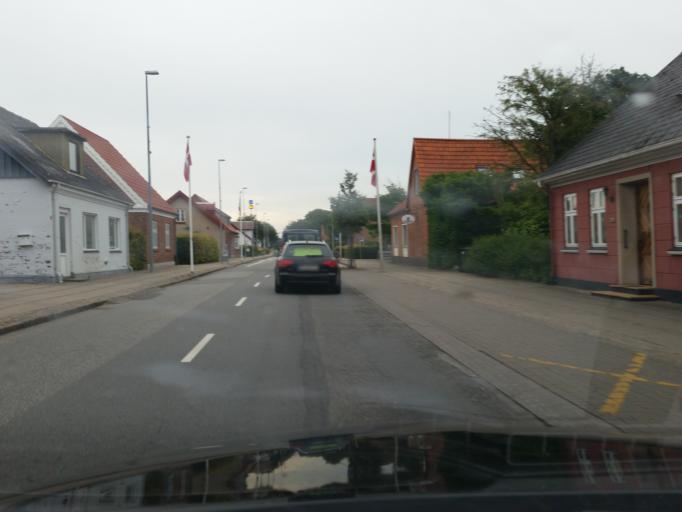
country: DK
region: South Denmark
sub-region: Varde Kommune
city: Oksbol
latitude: 55.7785
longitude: 8.2940
